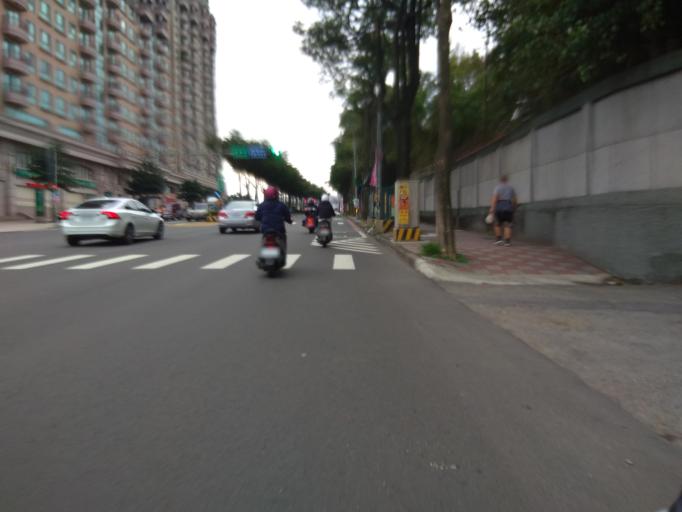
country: TW
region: Taiwan
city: Daxi
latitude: 24.9045
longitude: 121.2117
